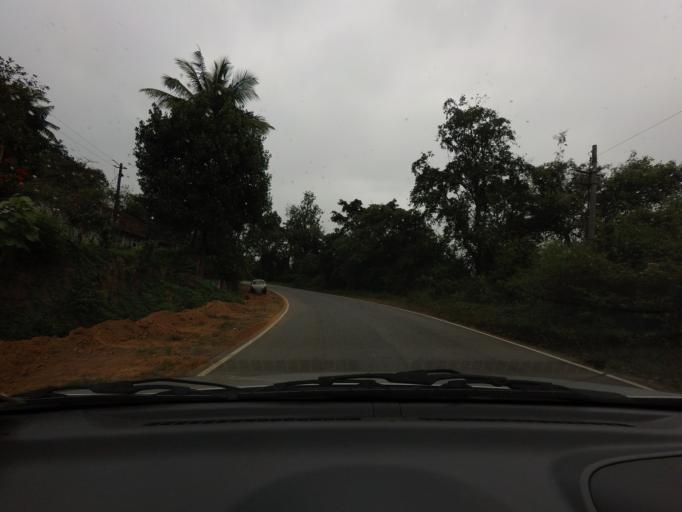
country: IN
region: Karnataka
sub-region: Hassan
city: Sakleshpur
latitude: 12.9522
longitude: 75.7502
